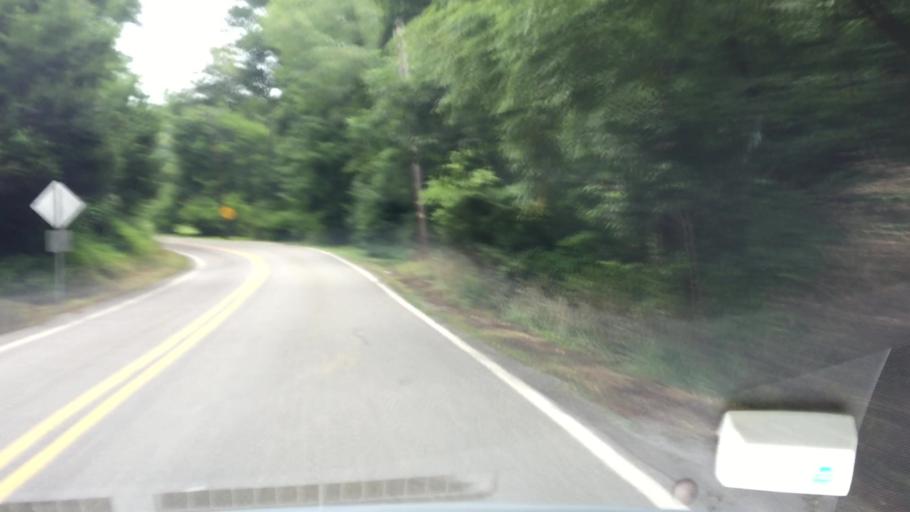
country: US
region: Pennsylvania
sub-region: Allegheny County
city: Allison Park
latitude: 40.5812
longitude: -79.9044
